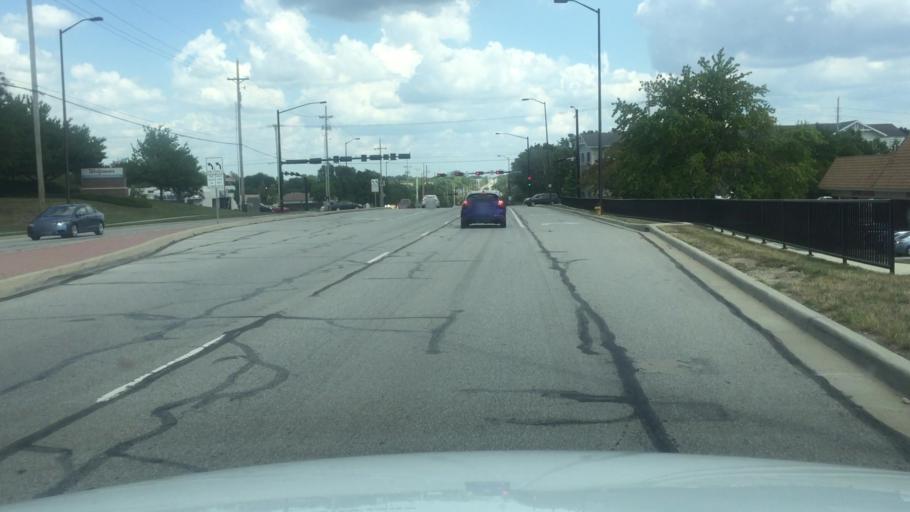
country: US
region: Kansas
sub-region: Johnson County
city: Lenexa
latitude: 38.9710
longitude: -94.7624
